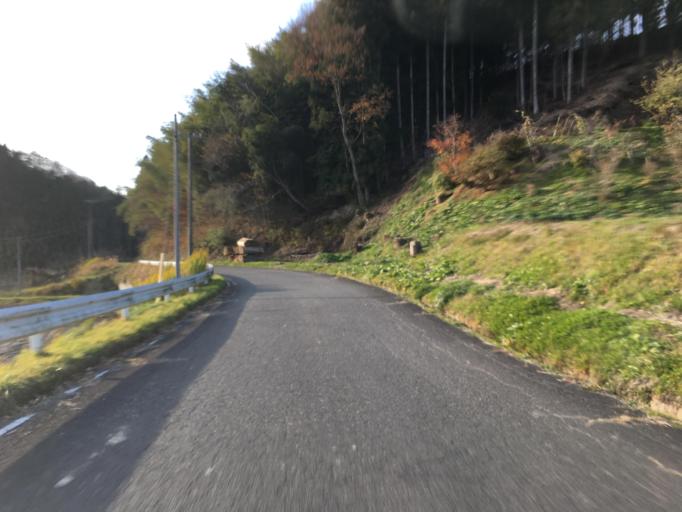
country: JP
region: Fukushima
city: Ishikawa
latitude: 37.2487
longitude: 140.5770
